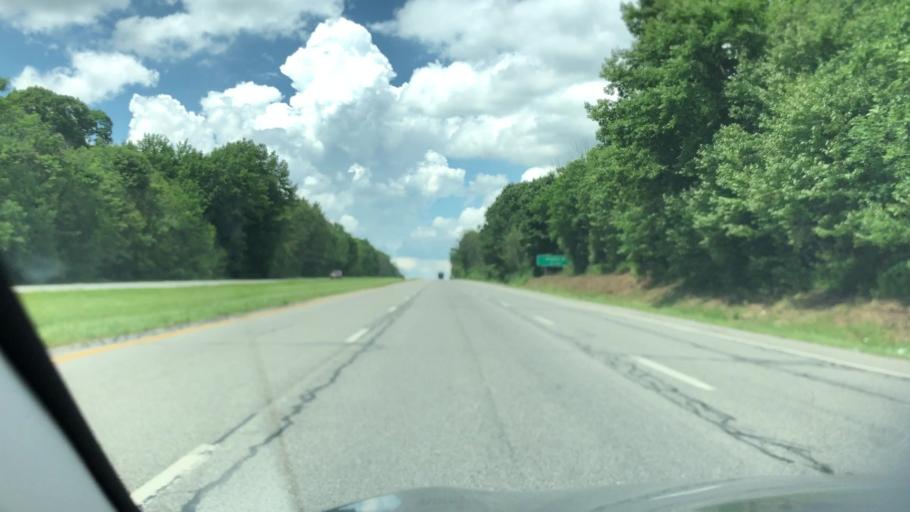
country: US
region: Ohio
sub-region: Stark County
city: Canal Fulton
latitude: 40.8793
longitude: -81.6079
